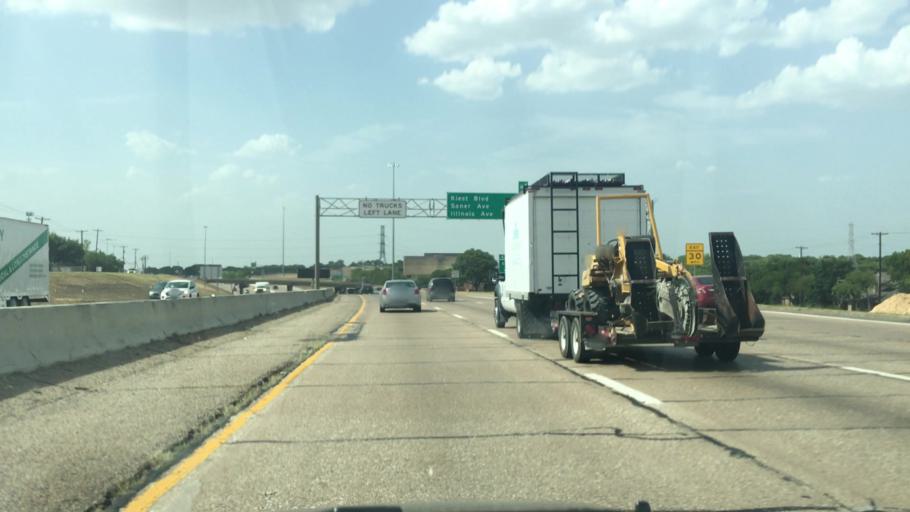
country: US
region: Texas
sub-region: Dallas County
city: Cockrell Hill
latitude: 32.6979
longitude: -96.8234
